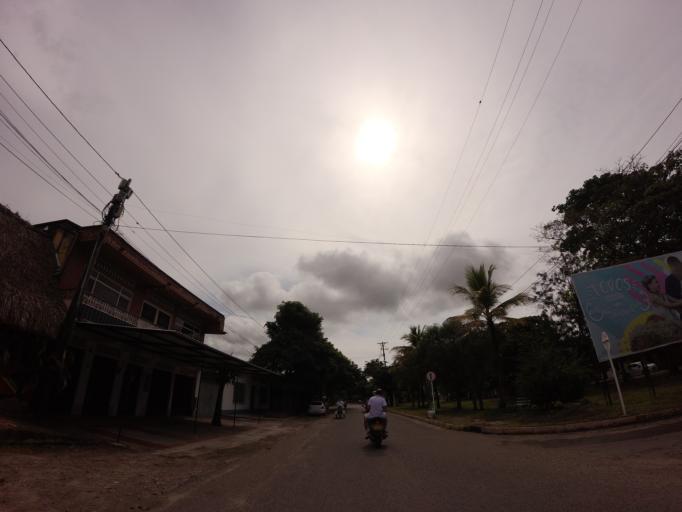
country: CO
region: Caldas
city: La Dorada
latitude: 5.4493
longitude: -74.6635
